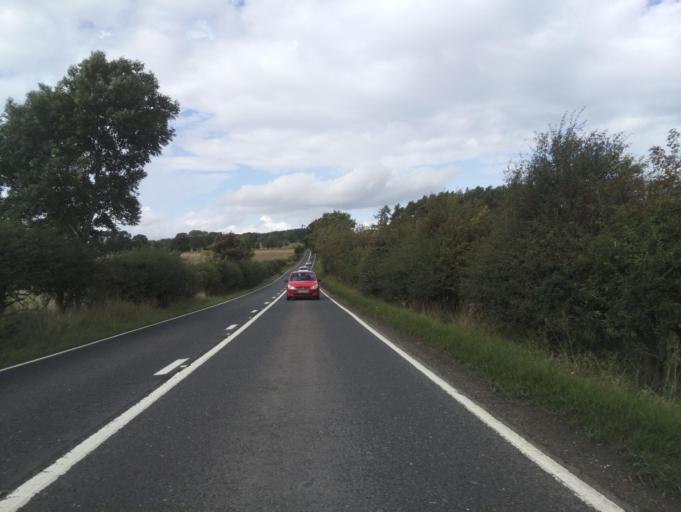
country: GB
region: England
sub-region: Northumberland
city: Acomb
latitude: 55.0557
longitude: -2.0648
